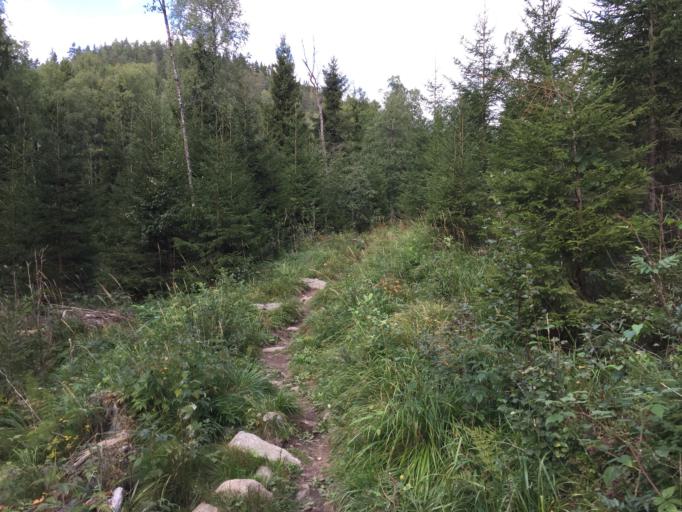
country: NO
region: Akershus
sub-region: Raelingen
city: Fjerdingby
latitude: 59.9104
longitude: 11.0376
